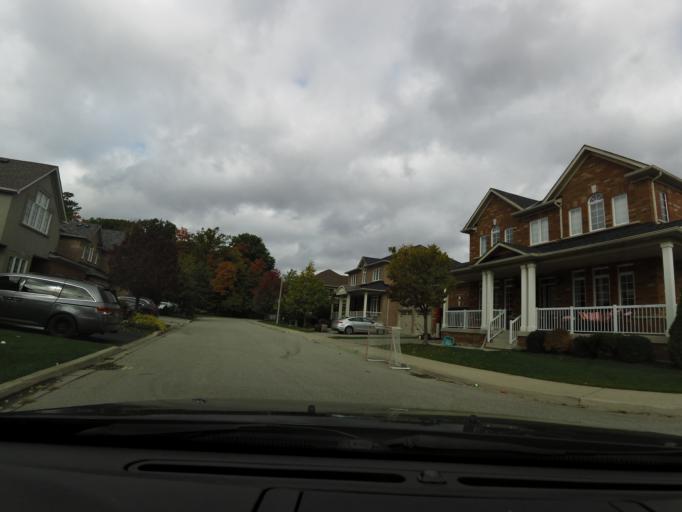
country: CA
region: Ontario
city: Burlington
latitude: 43.4032
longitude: -79.7877
